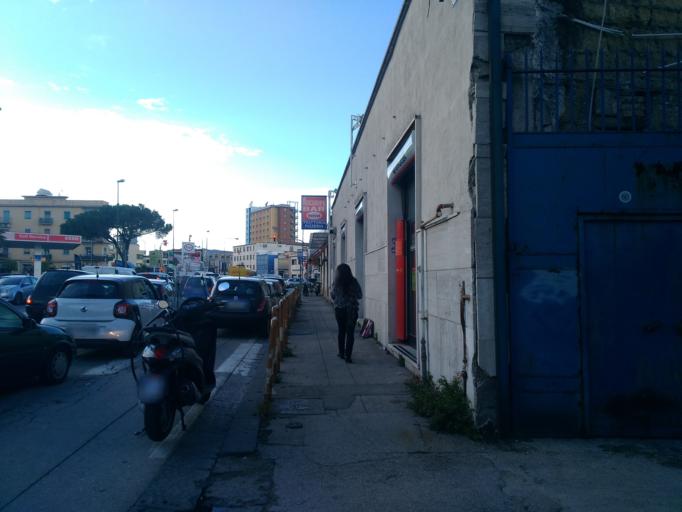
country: IT
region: Campania
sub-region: Provincia di Napoli
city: Napoli
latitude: 40.8495
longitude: 14.2903
